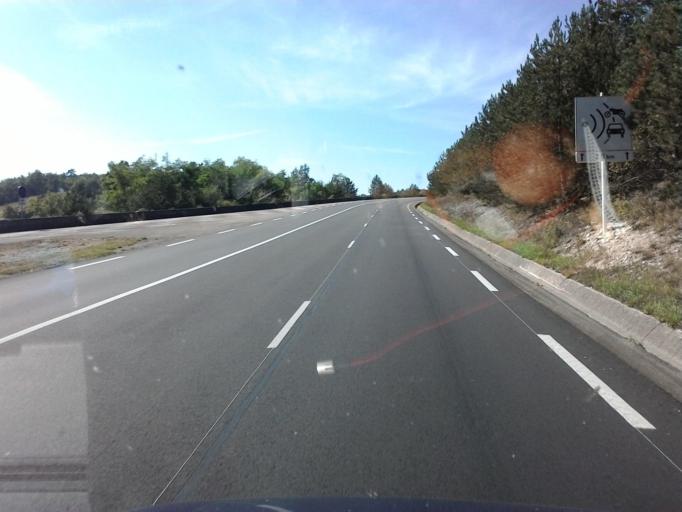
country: FR
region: Bourgogne
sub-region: Departement de l'Yonne
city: Tonnerre
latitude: 47.8481
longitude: 3.9835
